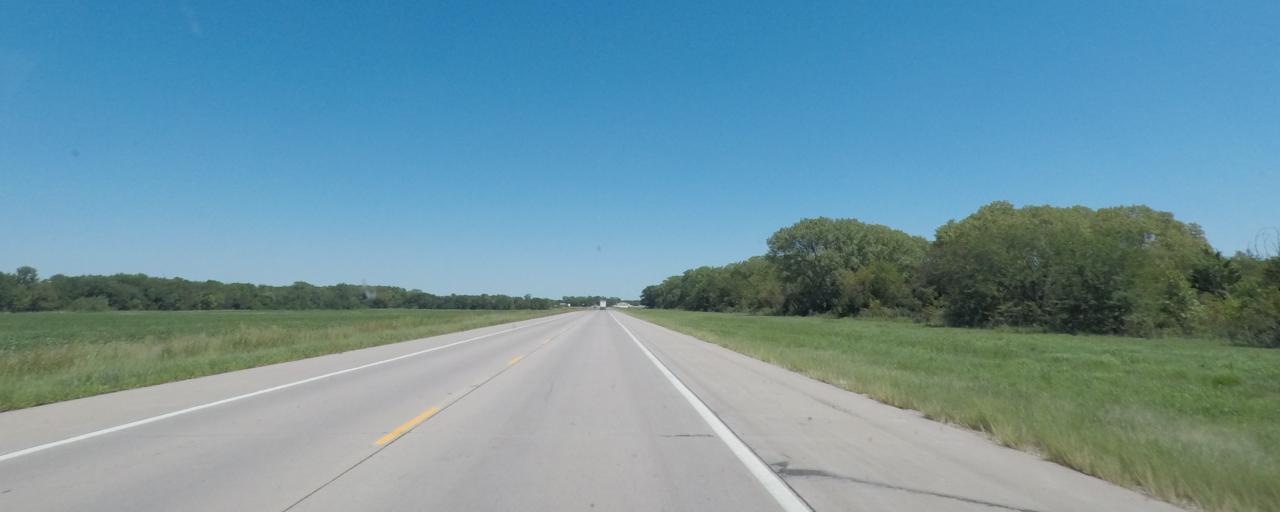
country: US
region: Kansas
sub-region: Lyon County
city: Emporia
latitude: 38.4065
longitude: -96.3168
